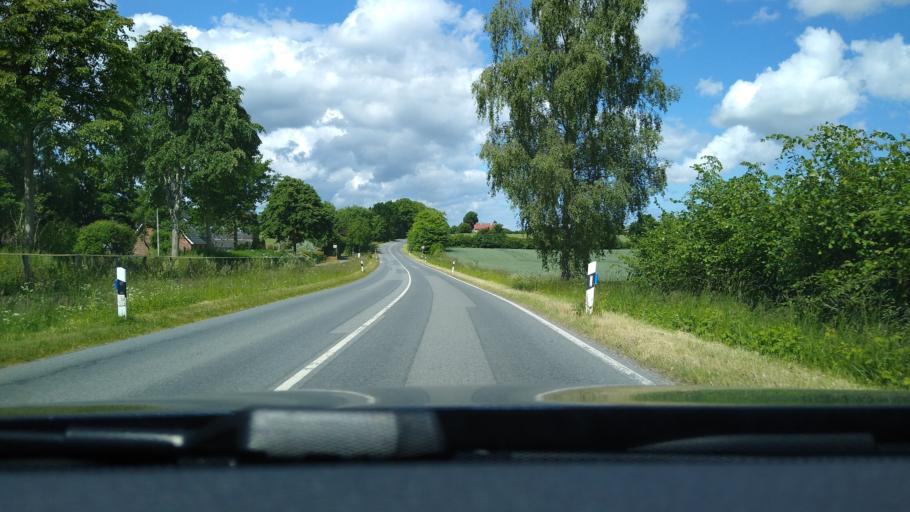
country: DE
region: Schleswig-Holstein
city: Riepsdorf
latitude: 54.1975
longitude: 10.9758
